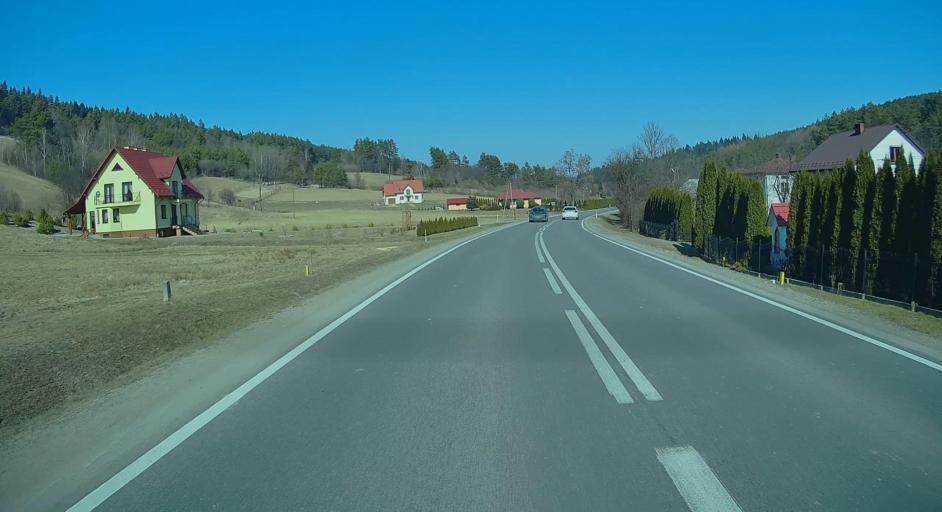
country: PL
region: Subcarpathian Voivodeship
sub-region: Powiat przemyski
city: Bircza
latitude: 49.6751
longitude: 22.4319
